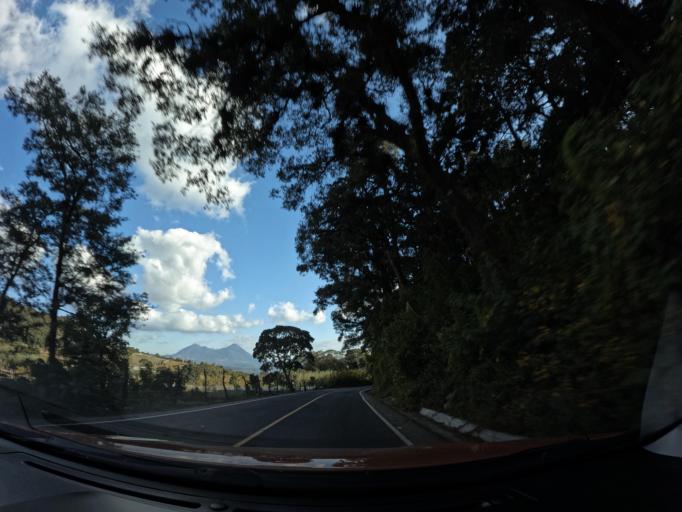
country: GT
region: Sacatepequez
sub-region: Municipio de Santa Maria de Jesus
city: Santa Maria de Jesus
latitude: 14.4734
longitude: -90.6933
